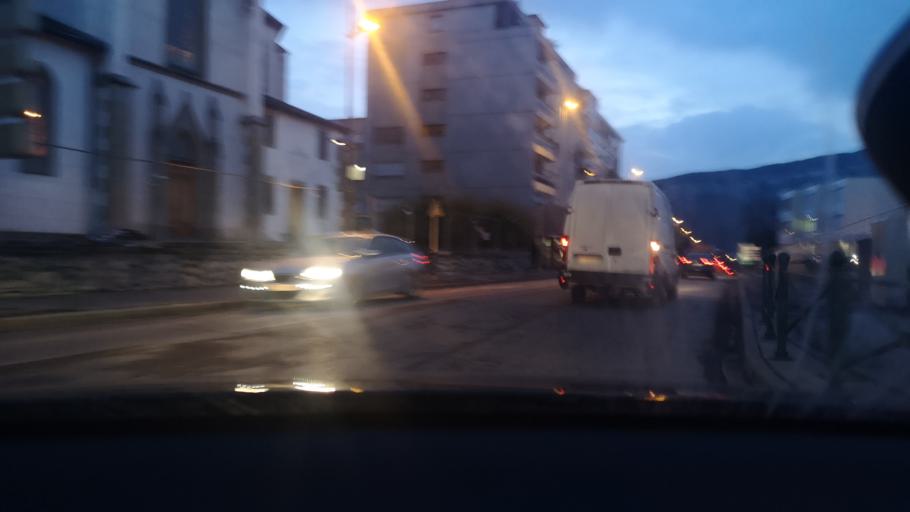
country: FR
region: Rhone-Alpes
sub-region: Departement de la Haute-Savoie
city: Annemasse
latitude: 46.1899
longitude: 6.2332
